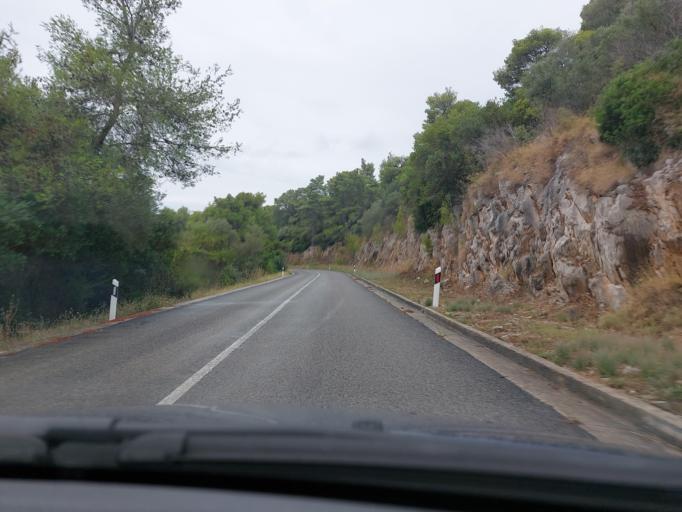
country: HR
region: Dubrovacko-Neretvanska
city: Smokvica
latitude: 42.7708
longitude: 16.8619
